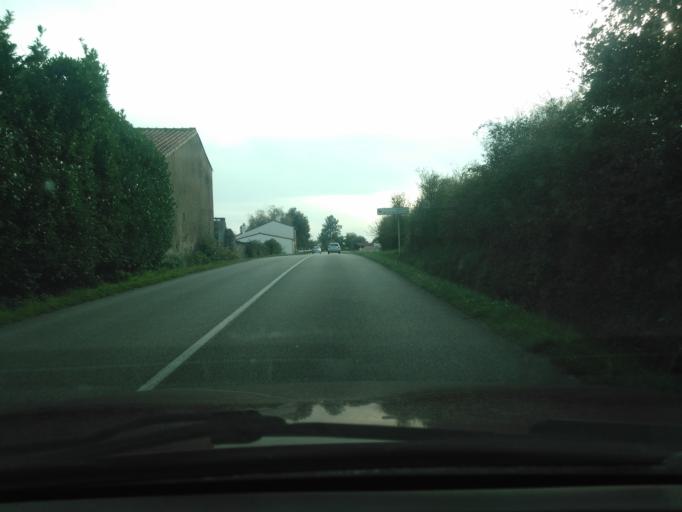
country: FR
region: Pays de la Loire
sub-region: Departement de la Vendee
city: Dompierre-sur-Yon
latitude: 46.7197
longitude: -1.4048
